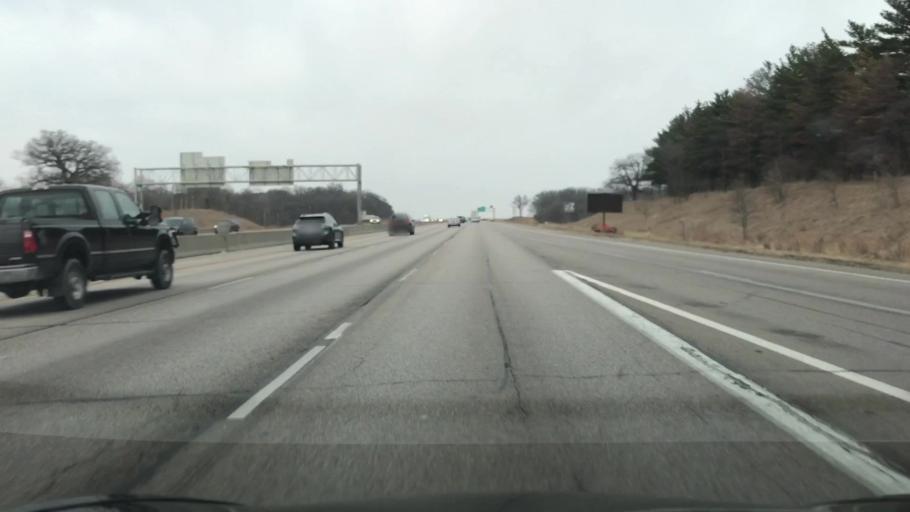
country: US
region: Iowa
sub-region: Polk County
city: Clive
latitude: 41.6187
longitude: -93.7766
